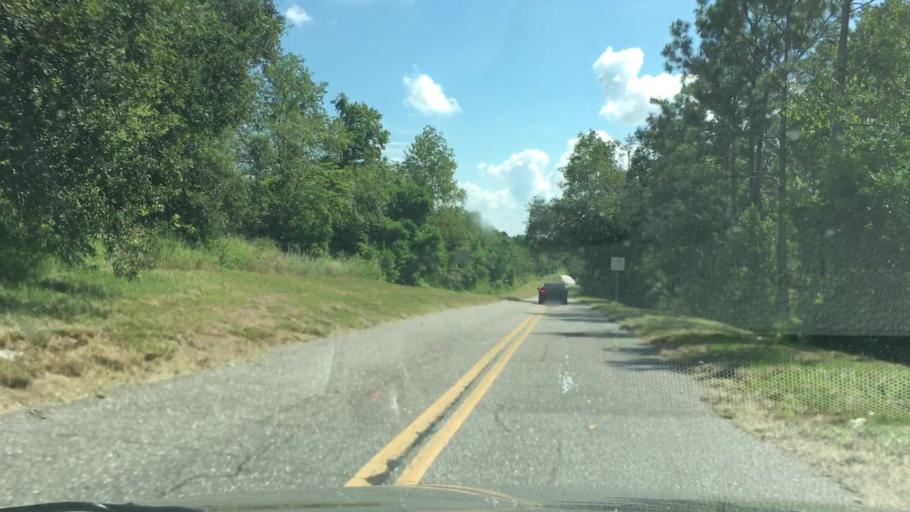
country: US
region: Florida
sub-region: Lake County
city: Montverde
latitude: 28.6375
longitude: -81.7173
